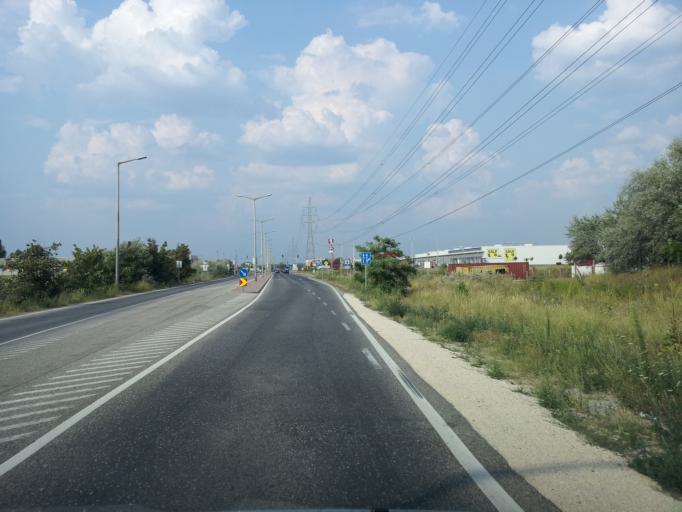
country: HU
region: Pest
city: Dunaharaszti
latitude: 47.3426
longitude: 19.1149
